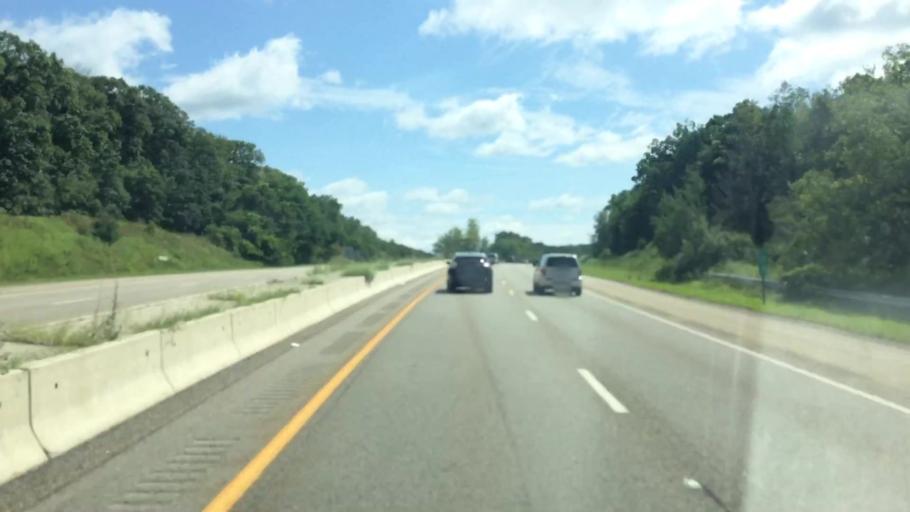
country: US
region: Rhode Island
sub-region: Providence County
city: Cumberland Hill
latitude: 41.9589
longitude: -71.4832
